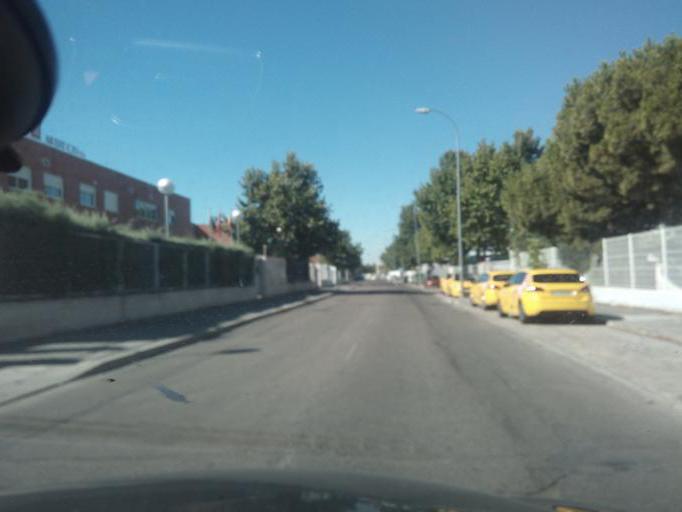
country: ES
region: Madrid
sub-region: Provincia de Madrid
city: Torrejon de Ardoz
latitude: 40.4528
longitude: -3.4860
